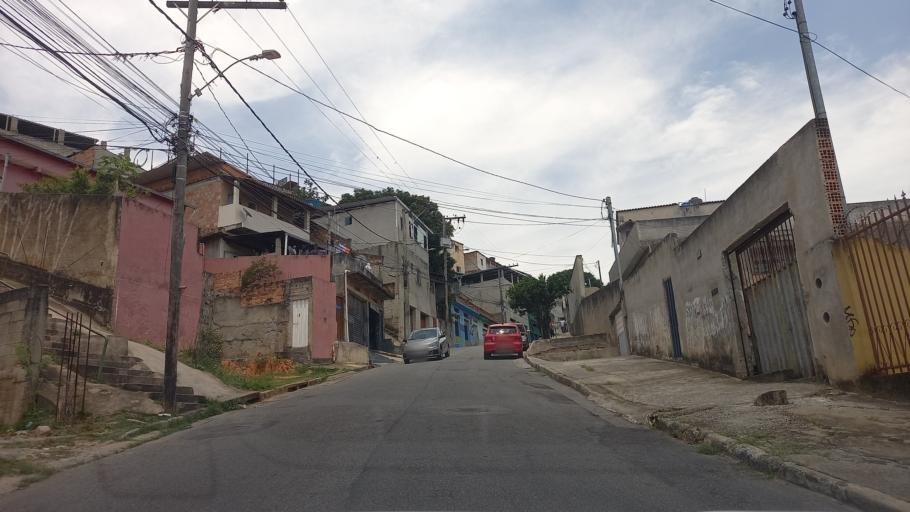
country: BR
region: Minas Gerais
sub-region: Contagem
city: Contagem
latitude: -19.9095
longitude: -44.0074
